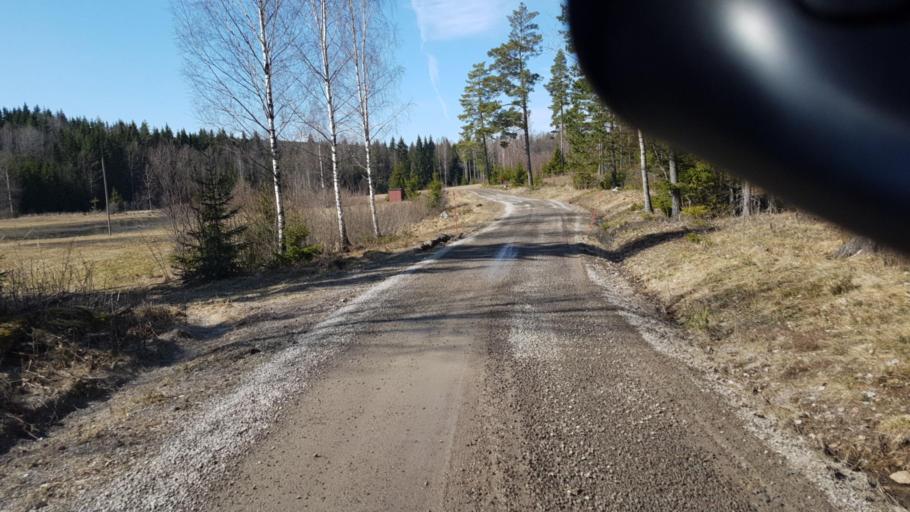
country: SE
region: Vaermland
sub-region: Arvika Kommun
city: Arvika
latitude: 59.5621
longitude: 12.8401
